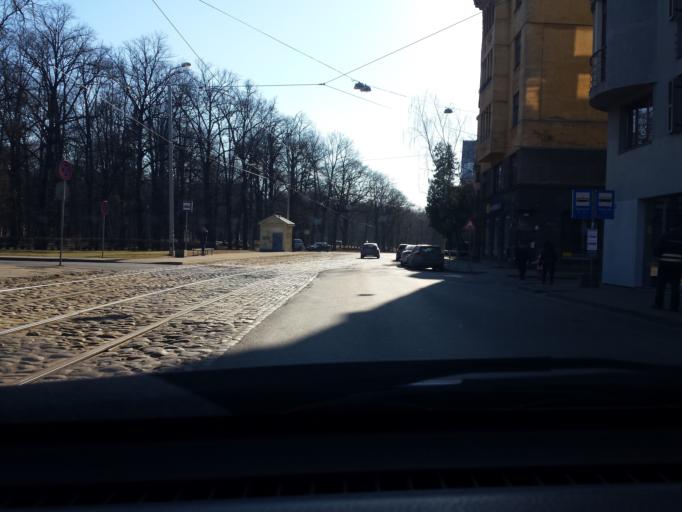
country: LV
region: Riga
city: Riga
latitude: 56.9734
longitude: 24.1420
